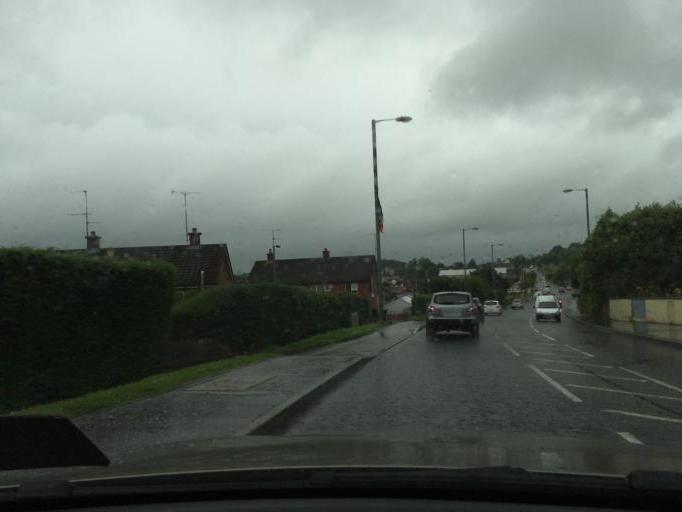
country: GB
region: Northern Ireland
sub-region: Fermanagh District
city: Enniskillen
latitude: 54.3545
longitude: -7.6368
